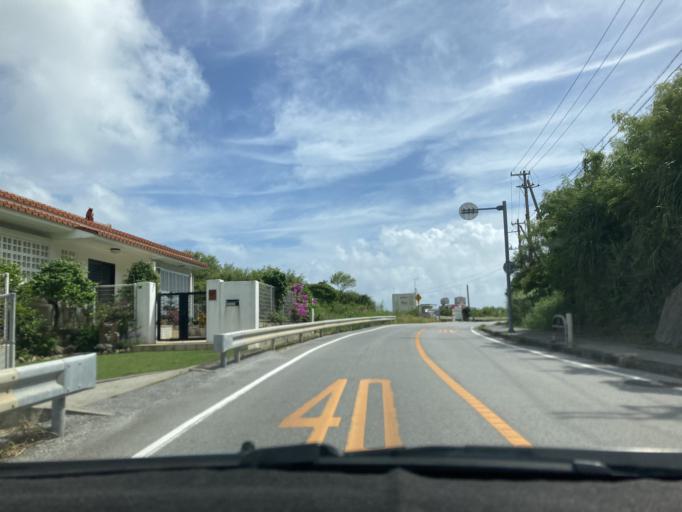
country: JP
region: Okinawa
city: Ginowan
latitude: 26.1762
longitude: 127.8280
